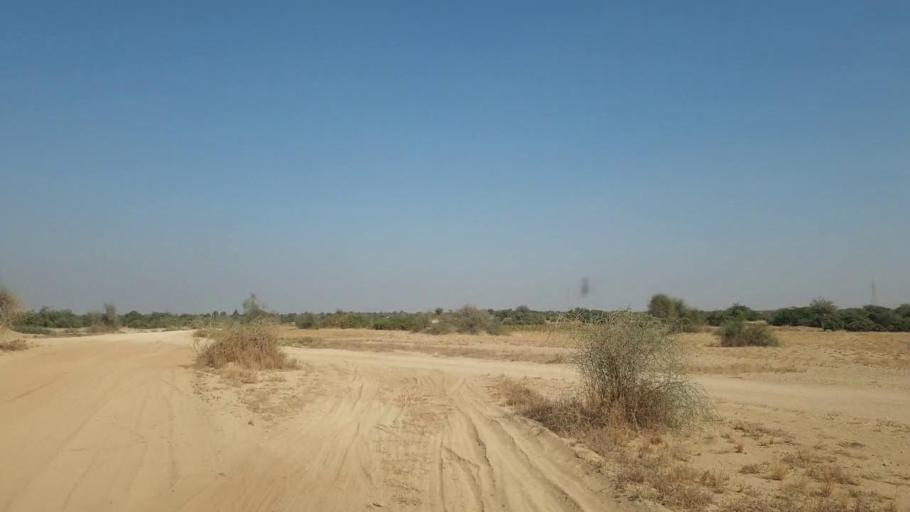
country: PK
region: Sindh
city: Jamshoro
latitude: 25.2800
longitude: 67.8076
